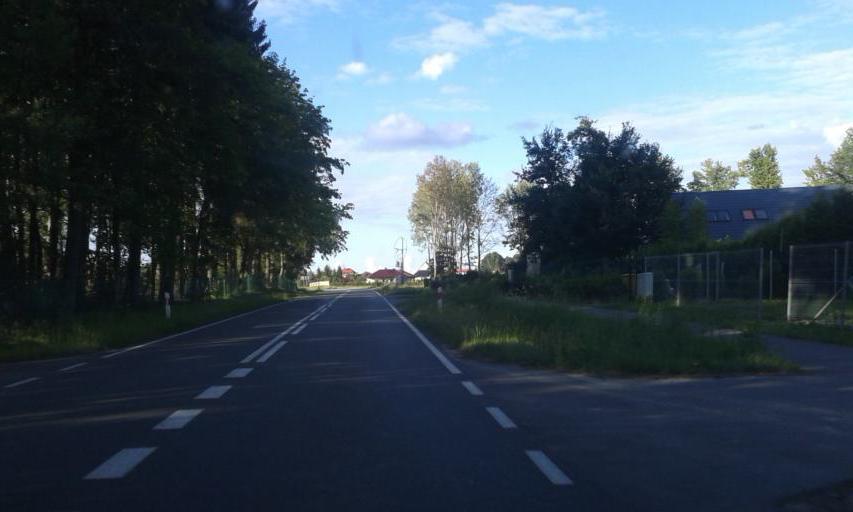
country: PL
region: West Pomeranian Voivodeship
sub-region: Koszalin
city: Koszalin
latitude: 54.1422
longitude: 16.1713
